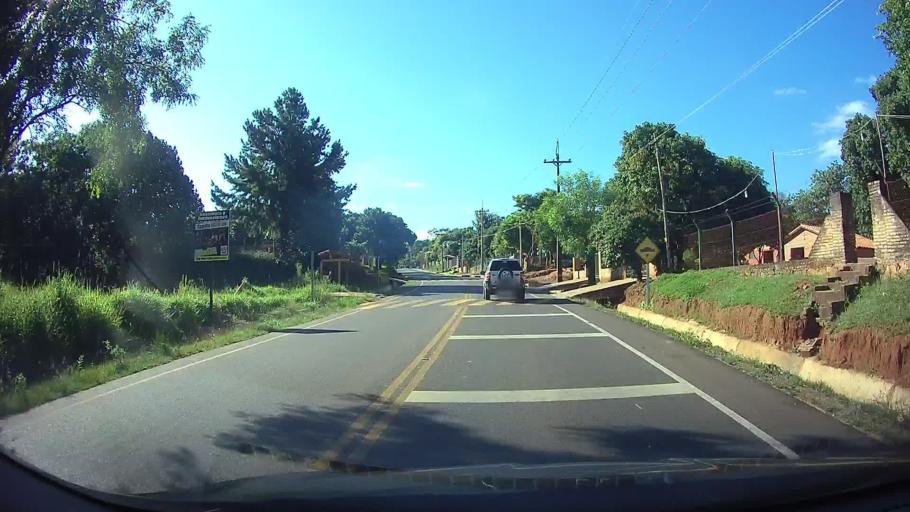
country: PY
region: Cordillera
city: Atyra
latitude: -25.3143
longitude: -57.1458
